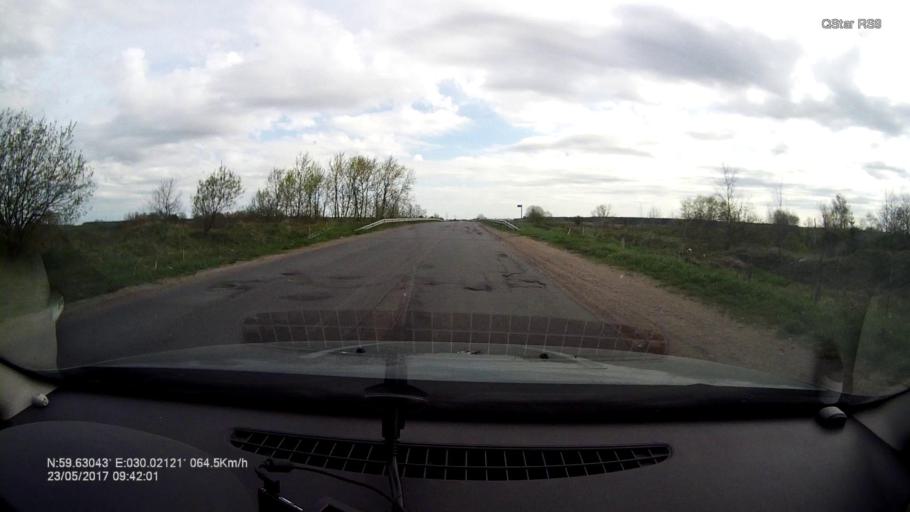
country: RU
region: Leningrad
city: Mariyenburg
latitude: 59.6306
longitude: 30.0215
